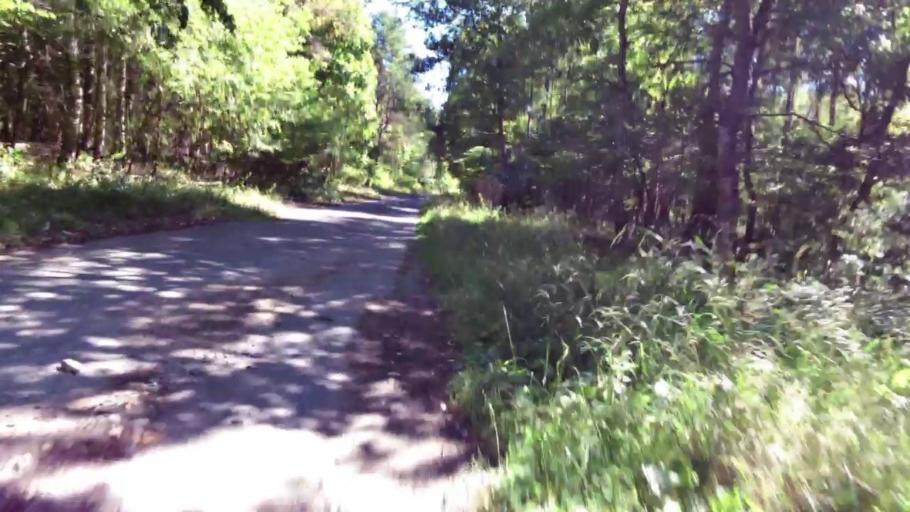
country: PL
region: West Pomeranian Voivodeship
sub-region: Powiat szczecinecki
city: Borne Sulinowo
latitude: 53.5986
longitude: 16.6235
